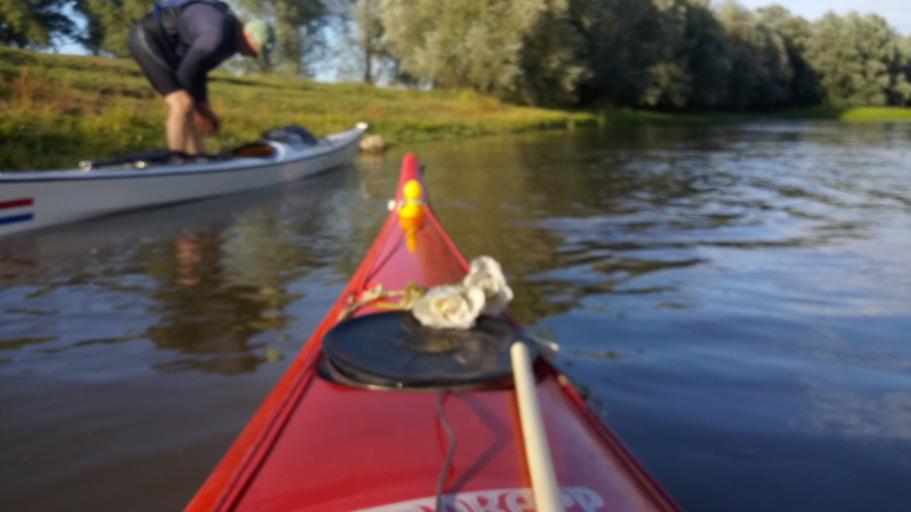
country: NL
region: Gelderland
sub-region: Gemeente Zaltbommel
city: Zaltbommel
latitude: 51.8055
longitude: 5.2114
